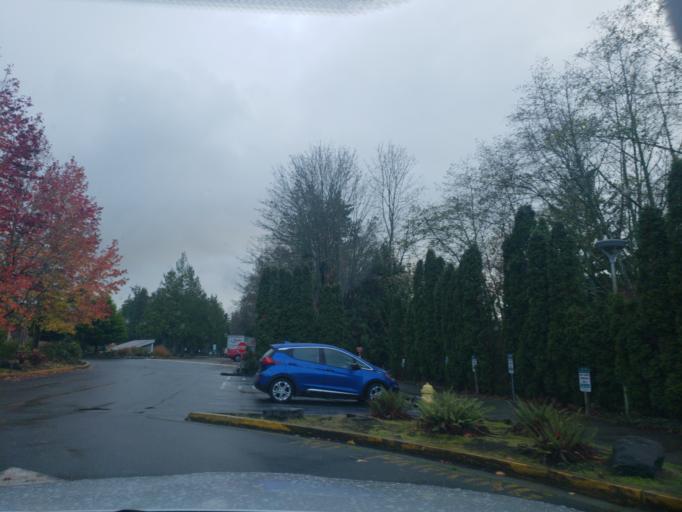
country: US
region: Washington
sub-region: King County
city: Shoreline
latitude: 47.7488
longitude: -122.3614
